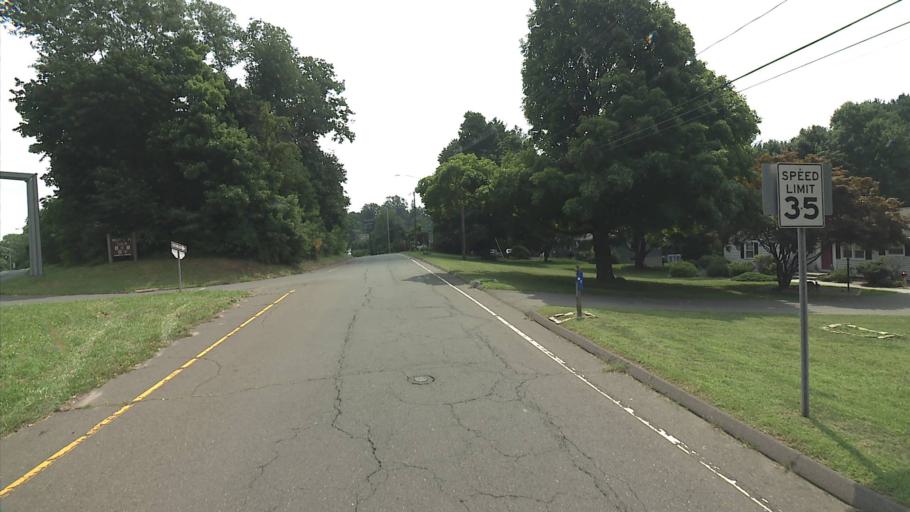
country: US
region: Connecticut
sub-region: Hartford County
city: New Britain
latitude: 41.6474
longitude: -72.7912
